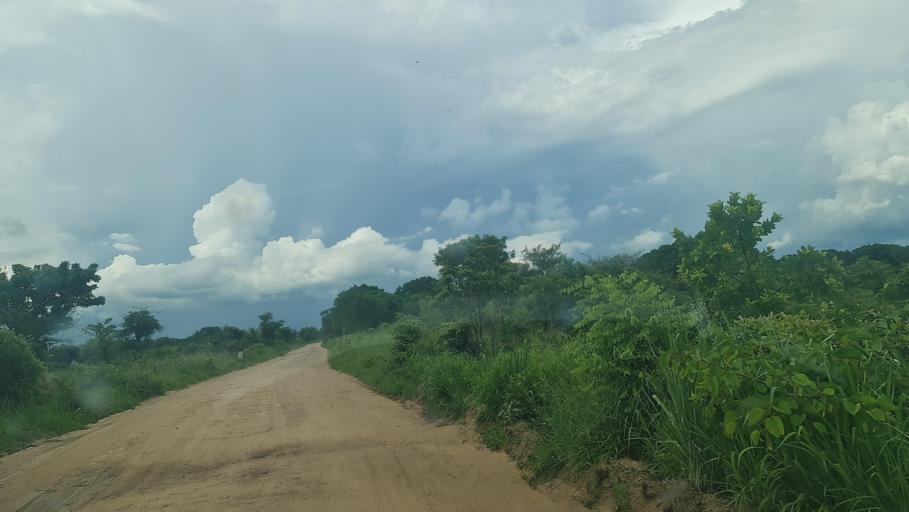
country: MW
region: Southern Region
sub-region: Nsanje District
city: Nsanje
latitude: -17.5961
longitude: 35.6748
